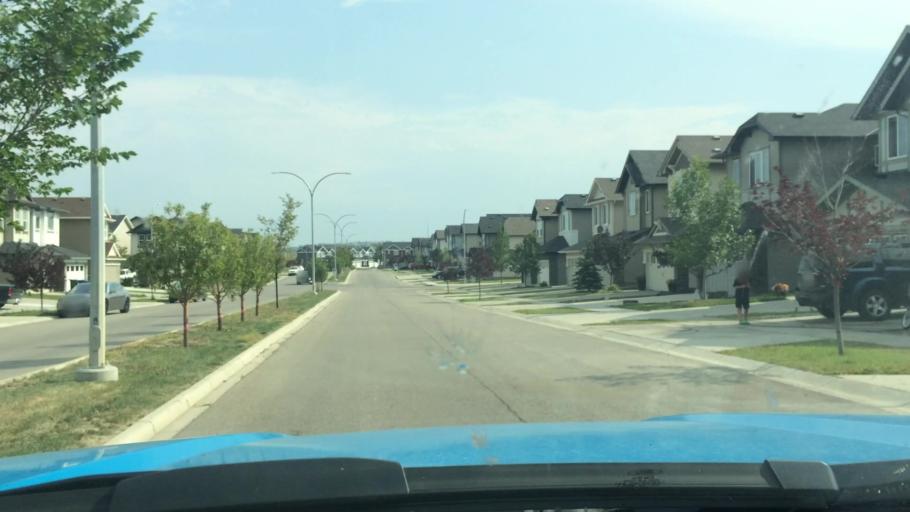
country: CA
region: Alberta
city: Calgary
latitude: 51.1784
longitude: -114.1543
